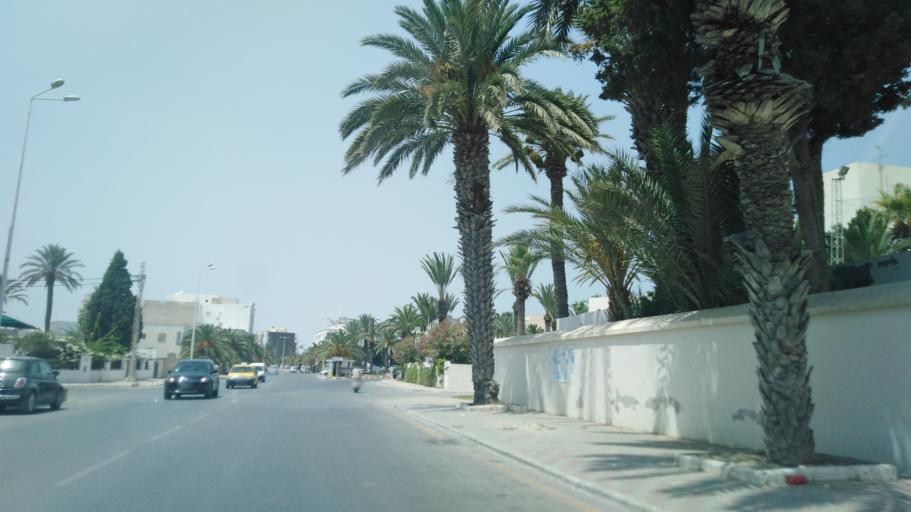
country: TN
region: Al Mahdiyah
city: Mahdia
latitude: 35.5166
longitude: 11.0445
